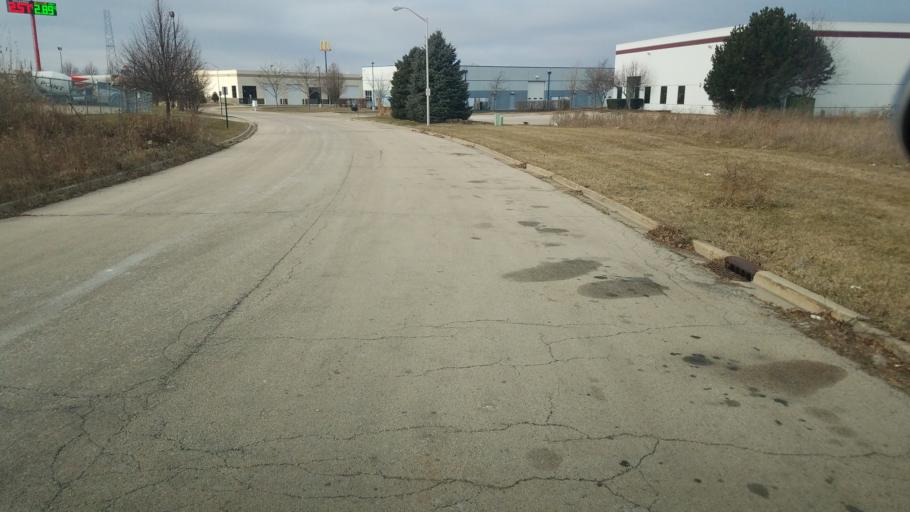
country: US
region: Illinois
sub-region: Kane County
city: Hampshire
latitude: 42.1491
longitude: -88.5068
